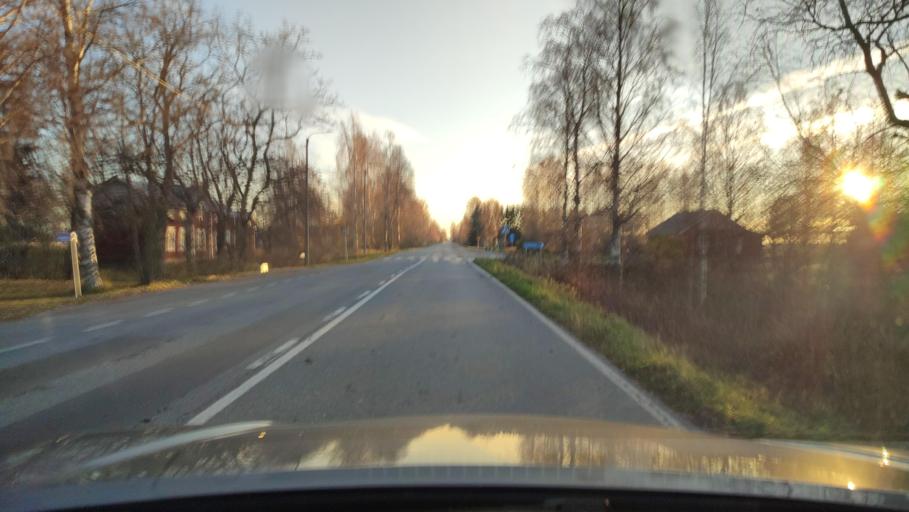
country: FI
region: Ostrobothnia
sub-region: Sydosterbotten
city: Naerpes
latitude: 62.5507
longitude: 21.4025
